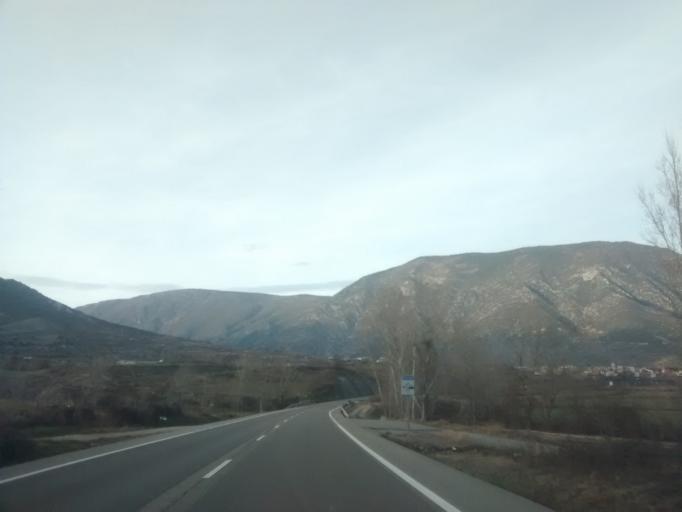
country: ES
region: Catalonia
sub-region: Provincia de Lleida
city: Coll de Nargo
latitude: 42.1955
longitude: 1.3286
